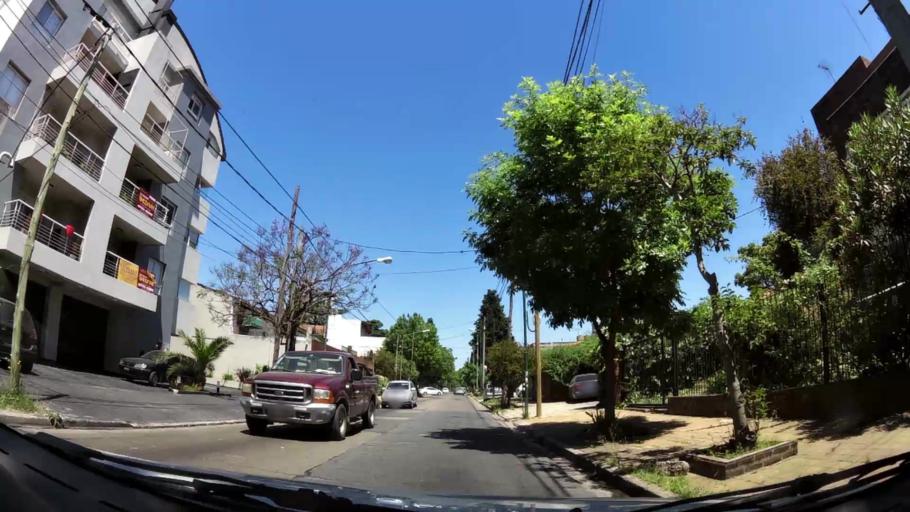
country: AR
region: Buenos Aires
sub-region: Partido de Vicente Lopez
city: Olivos
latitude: -34.5062
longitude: -58.5163
